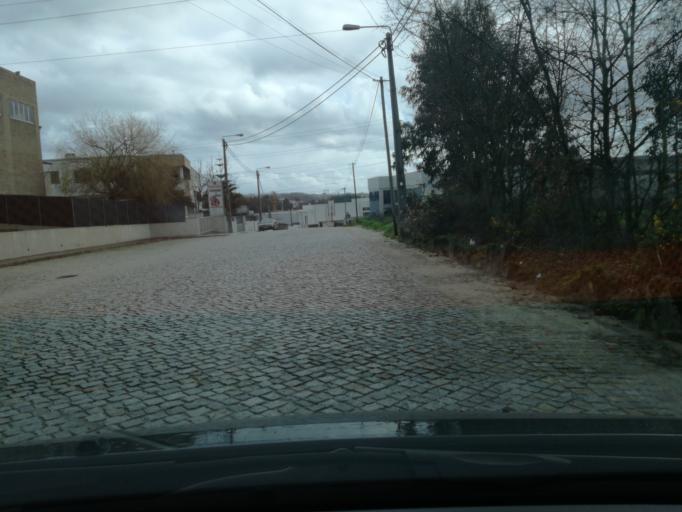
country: PT
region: Porto
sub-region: Valongo
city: Ermesinde
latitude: 41.2379
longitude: -8.5474
